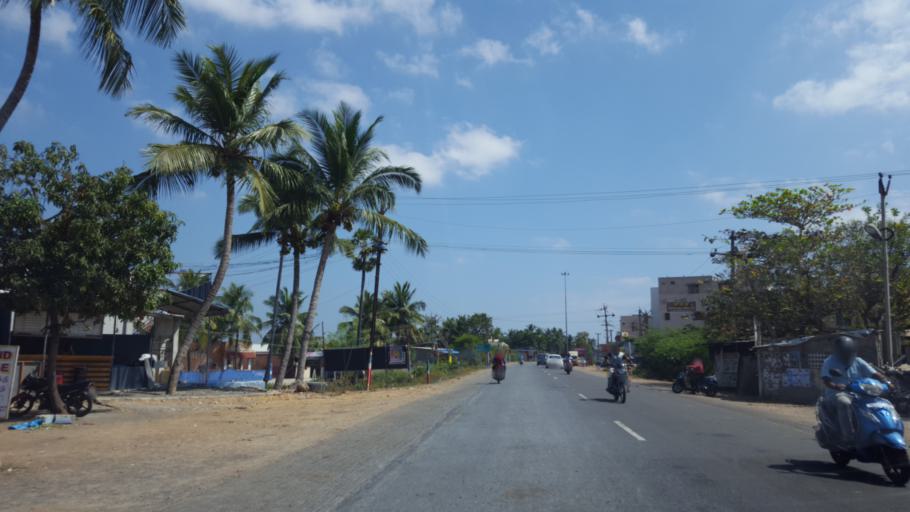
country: IN
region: Tamil Nadu
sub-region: Kancheepuram
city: Mamallapuram
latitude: 12.6169
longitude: 80.1754
